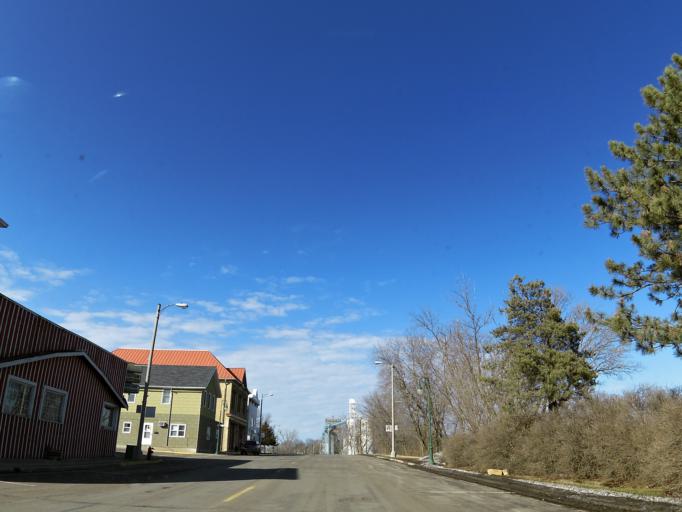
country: US
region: Minnesota
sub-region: Le Sueur County
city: Montgomery
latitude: 44.4395
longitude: -93.5811
